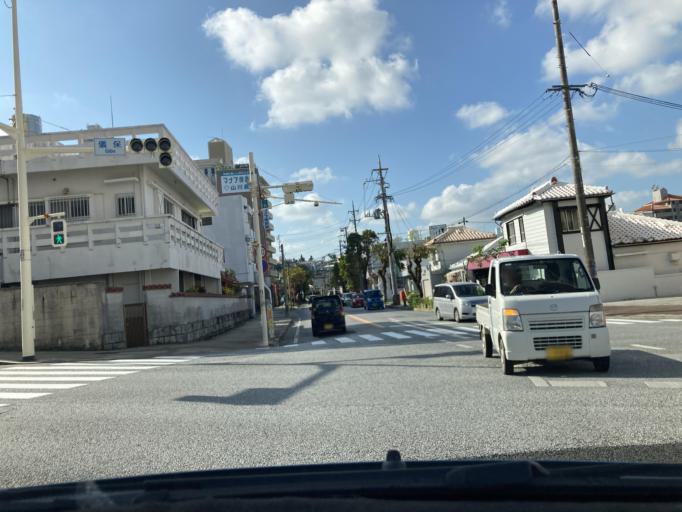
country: JP
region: Okinawa
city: Naha-shi
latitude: 26.2250
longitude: 127.7183
